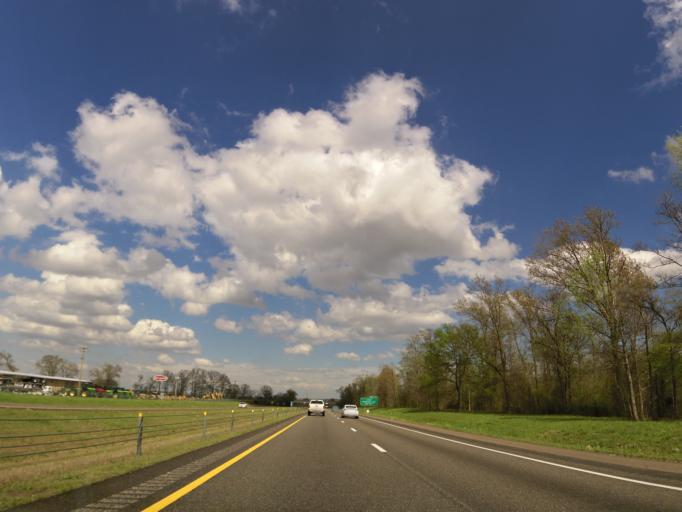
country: US
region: Tennessee
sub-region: Madison County
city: Jackson
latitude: 35.6312
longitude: -88.9555
